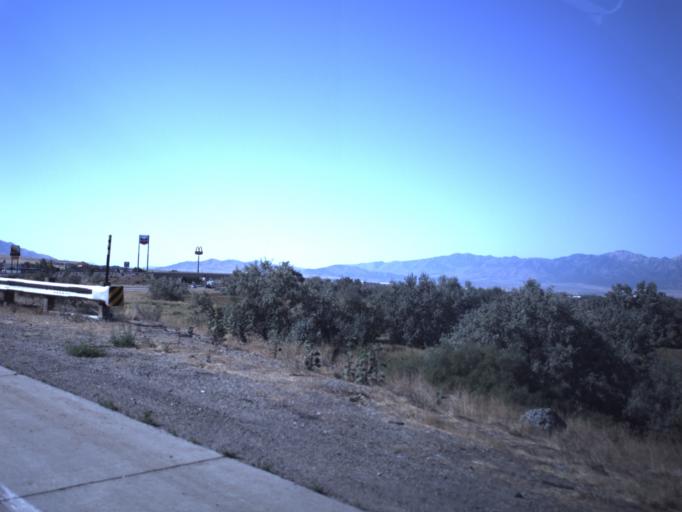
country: US
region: Utah
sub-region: Tooele County
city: Stansbury park
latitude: 40.6946
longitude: -112.2642
